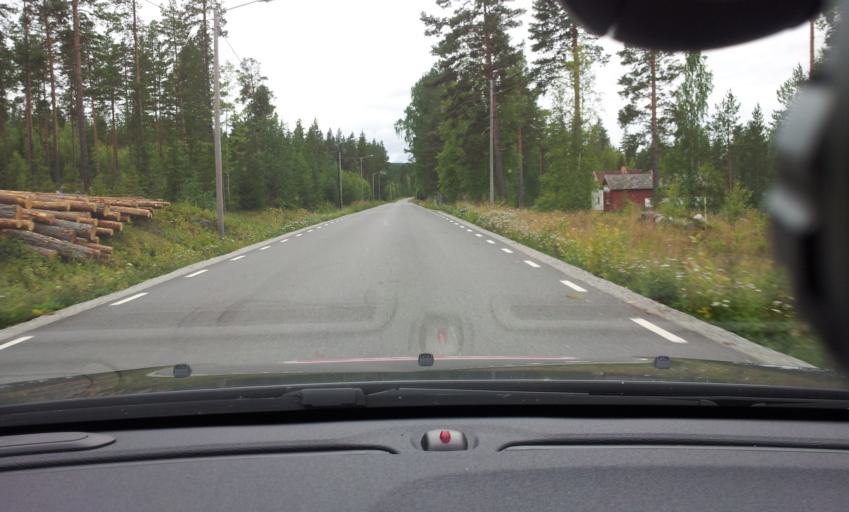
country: SE
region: Jaemtland
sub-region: Braecke Kommun
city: Braecke
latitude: 63.1528
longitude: 15.5532
